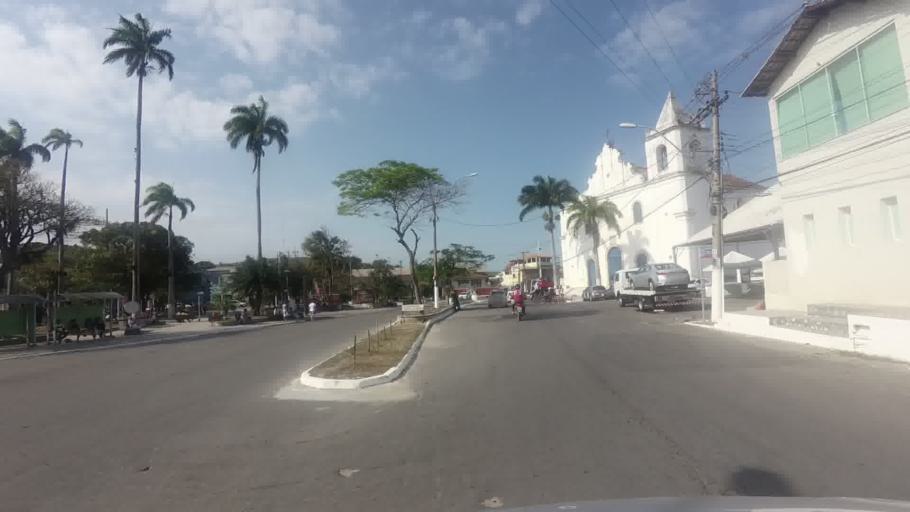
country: BR
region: Espirito Santo
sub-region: Itapemirim
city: Itapemirim
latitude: -21.0096
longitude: -40.8333
